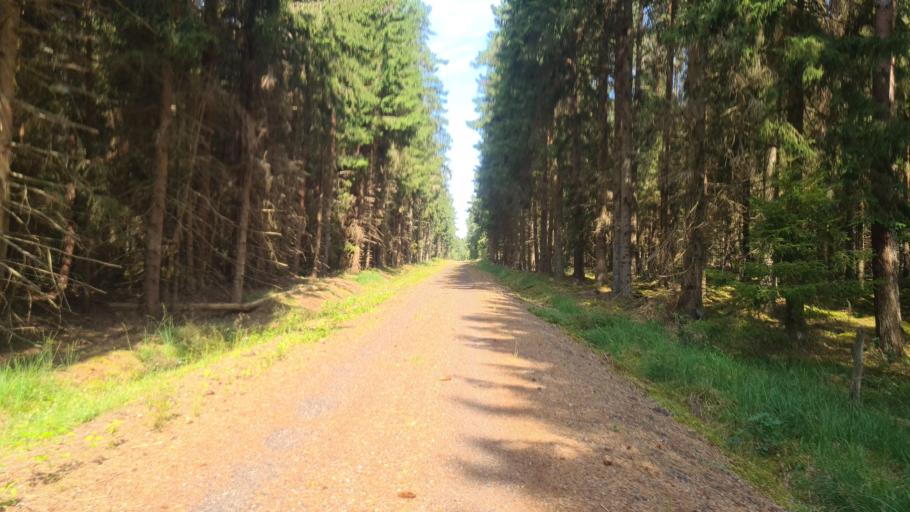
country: SE
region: Kronoberg
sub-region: Ljungby Kommun
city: Lagan
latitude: 56.9516
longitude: 13.9614
